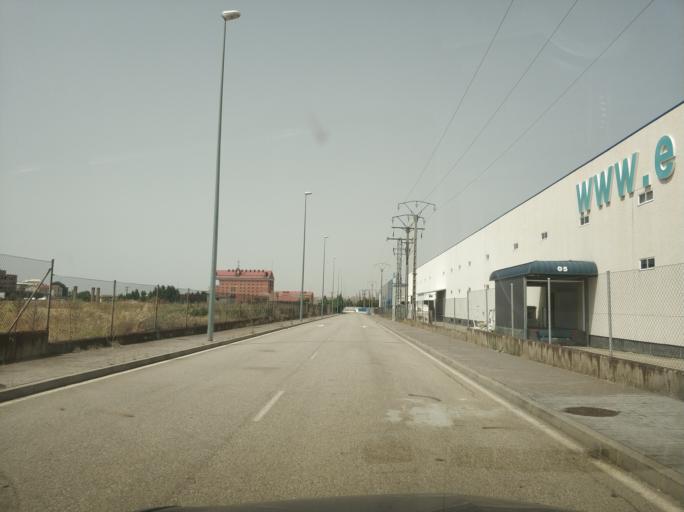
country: ES
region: Castille and Leon
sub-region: Provincia de Salamanca
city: Carbajosa de la Sagrada
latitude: 40.9440
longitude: -5.6670
